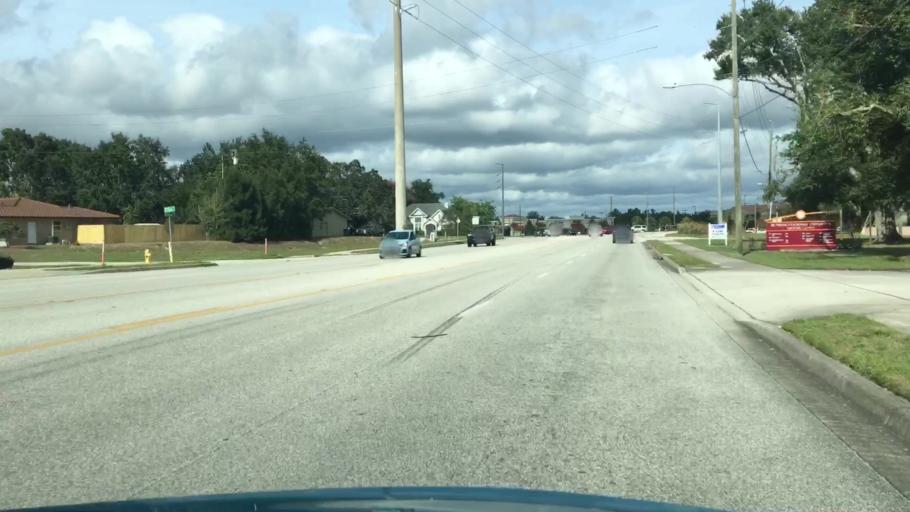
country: US
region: Florida
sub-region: Volusia County
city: Deltona
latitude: 28.9044
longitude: -81.2456
